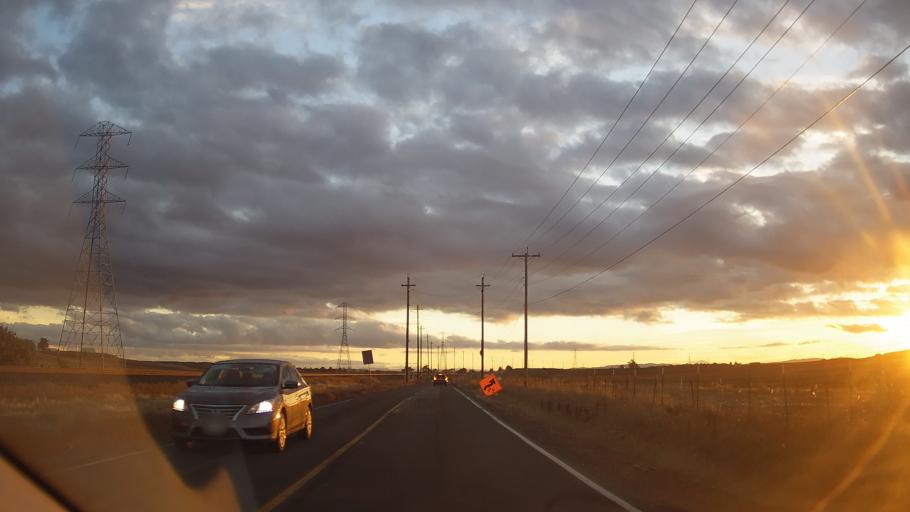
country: US
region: California
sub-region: Solano County
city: Vacaville
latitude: 38.3000
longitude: -121.9506
